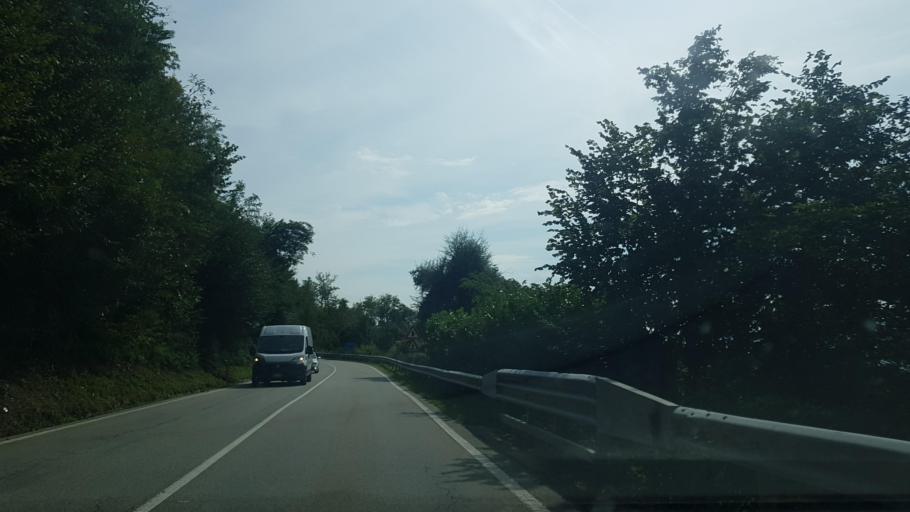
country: IT
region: Piedmont
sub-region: Provincia Verbano-Cusio-Ossola
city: Vignone
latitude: 45.9618
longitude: 8.5683
